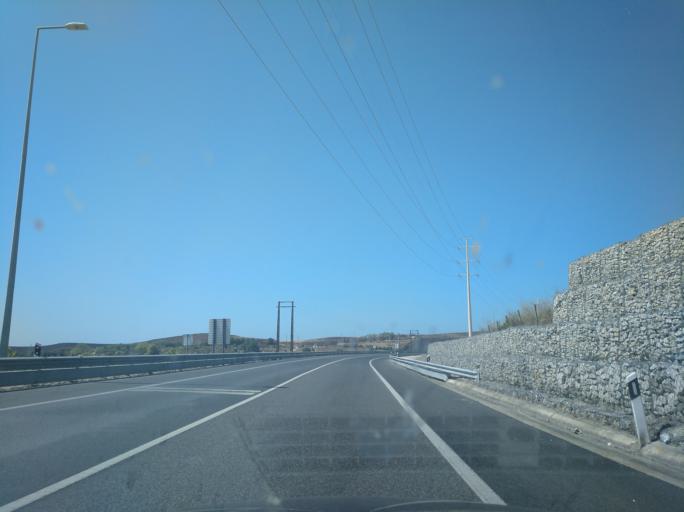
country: PT
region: Setubal
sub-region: Almada
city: Costa de Caparica
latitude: 38.6562
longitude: -9.2208
